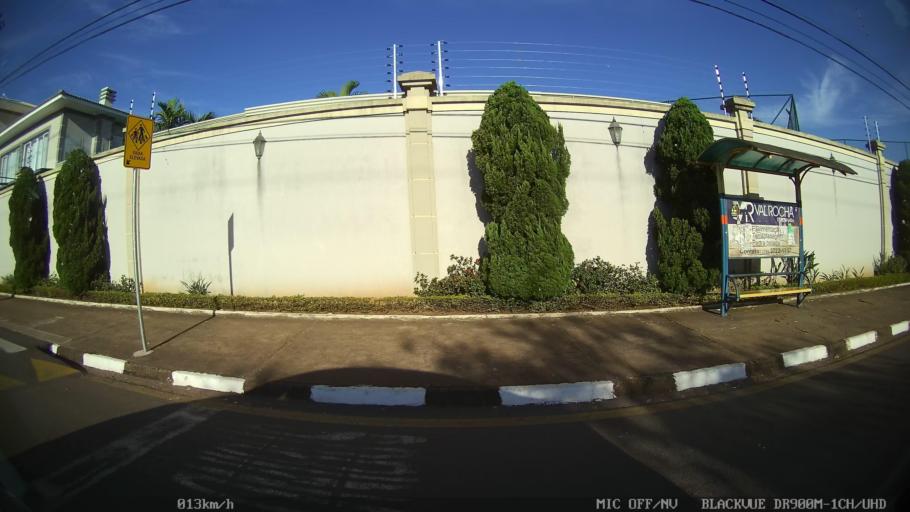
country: BR
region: Sao Paulo
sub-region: Franca
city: Franca
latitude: -20.5144
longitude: -47.3780
